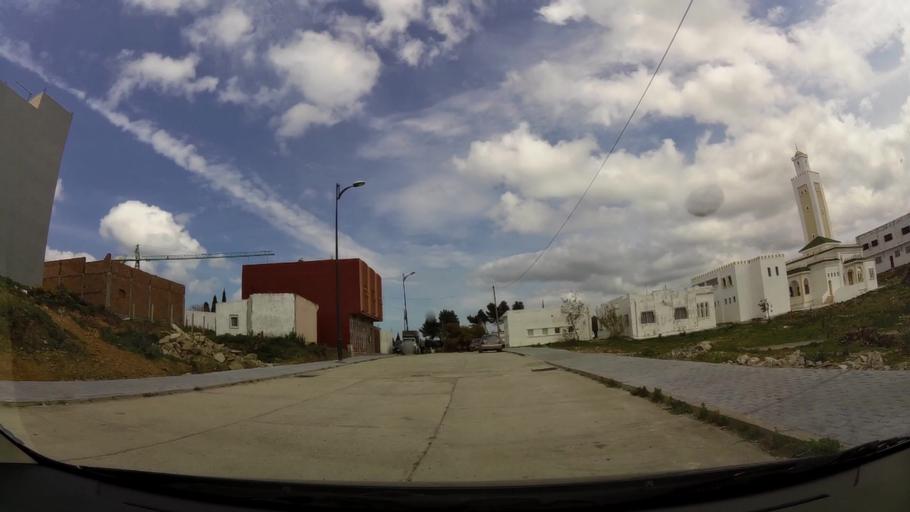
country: MA
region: Tanger-Tetouan
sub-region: Tanger-Assilah
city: Tangier
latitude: 35.7743
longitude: -5.7503
